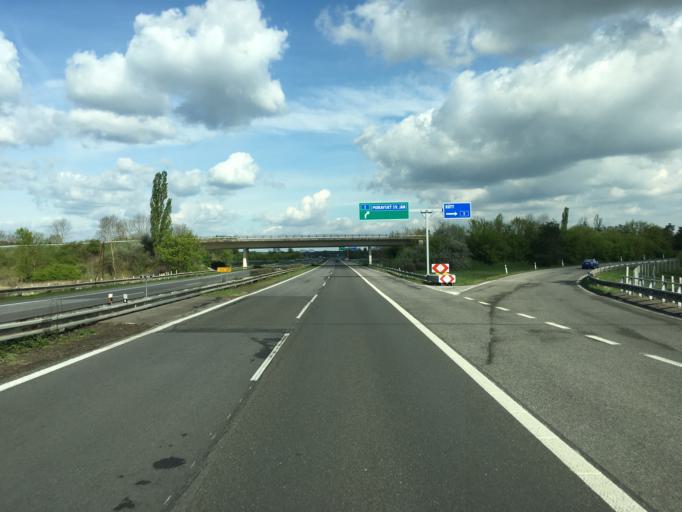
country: CZ
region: South Moravian
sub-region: Okres Breclav
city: Lanzhot
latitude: 48.6379
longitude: 17.0026
